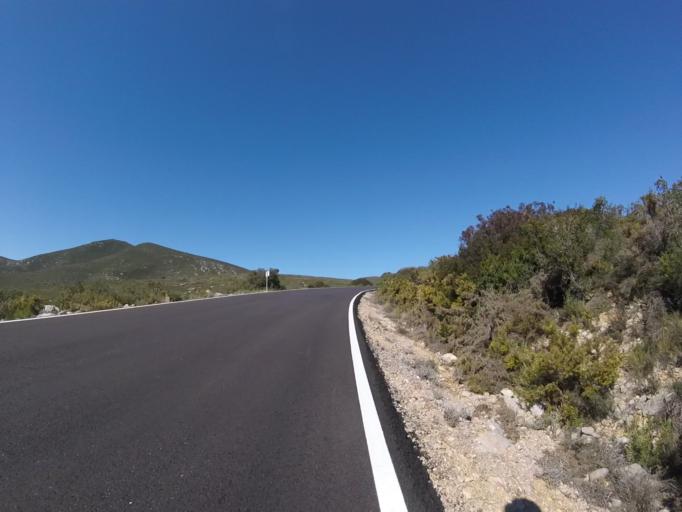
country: ES
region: Valencia
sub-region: Provincia de Castello
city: Cervera del Maestre
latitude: 40.4010
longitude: 0.2320
